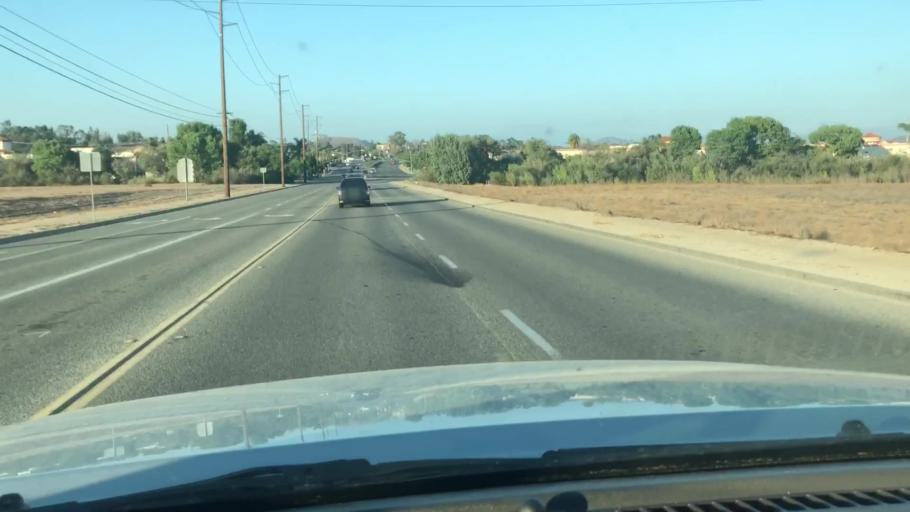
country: US
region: California
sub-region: Riverside County
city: Murrieta
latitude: 33.5510
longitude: -117.1985
